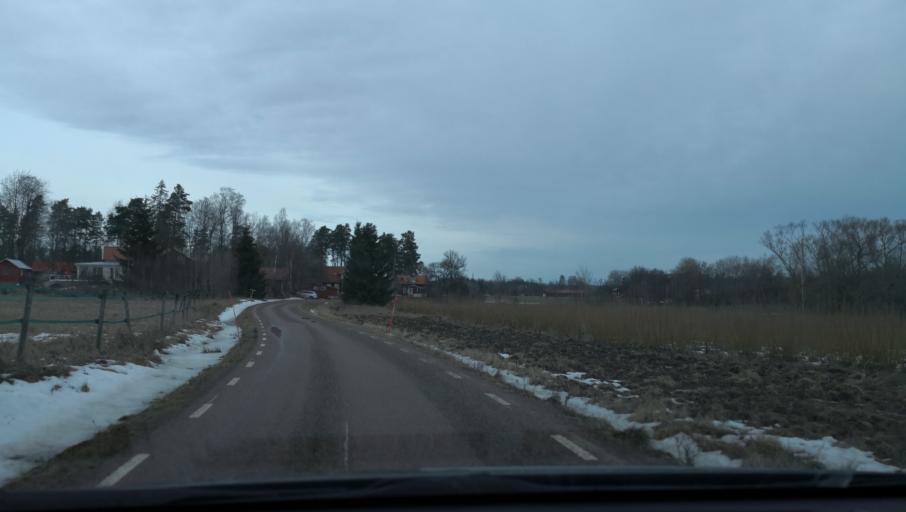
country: SE
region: Vaestmanland
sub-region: Vasteras
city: Skultuna
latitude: 59.6153
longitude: 16.4095
